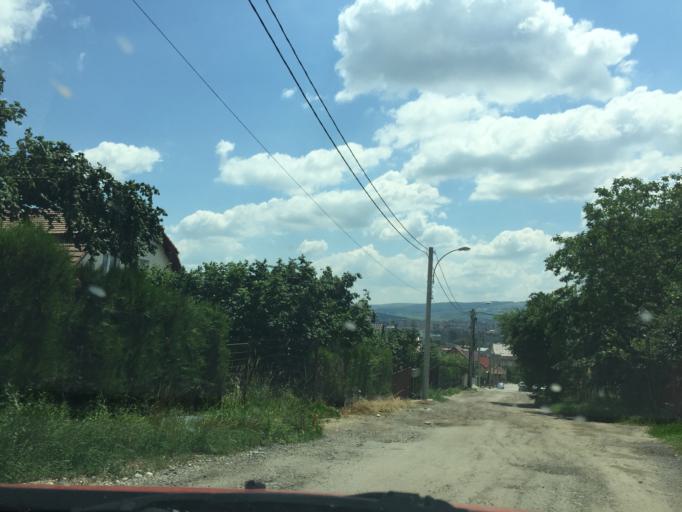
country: RO
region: Cluj
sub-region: Municipiul Cluj-Napoca
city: Cluj-Napoca
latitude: 46.7989
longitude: 23.6018
